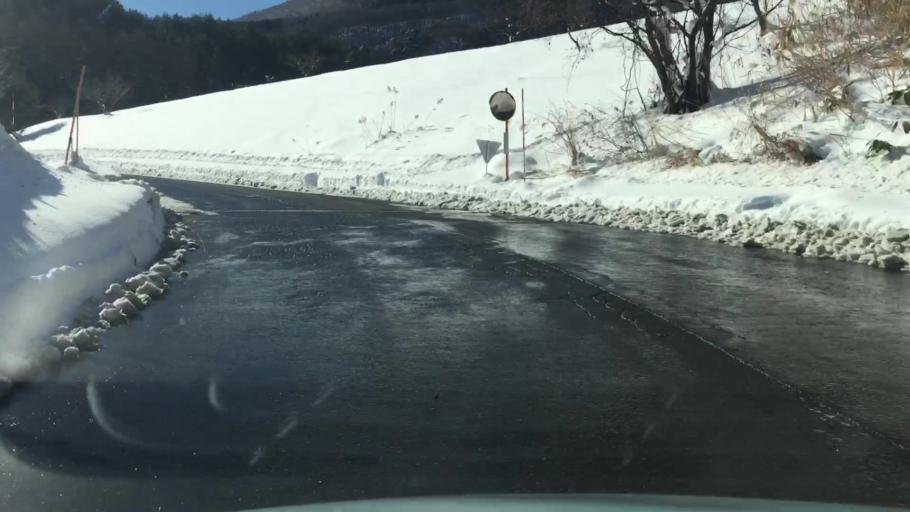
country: JP
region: Gunma
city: Numata
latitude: 36.7449
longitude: 138.9439
